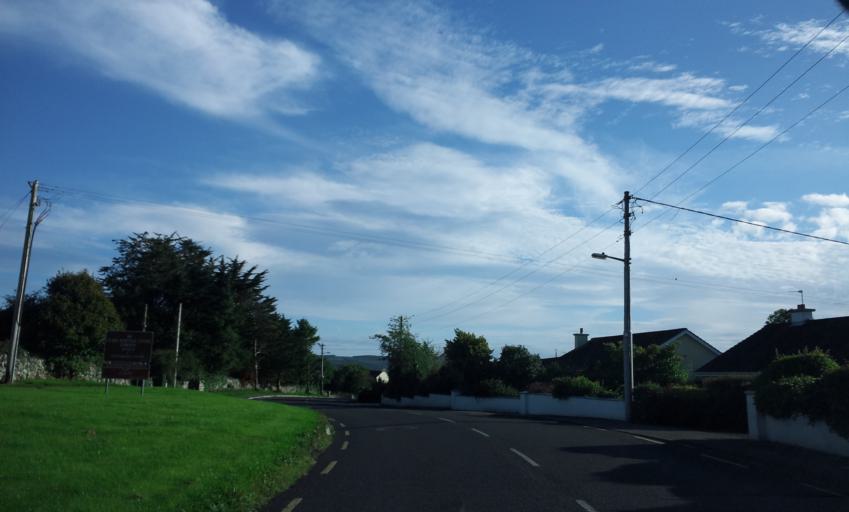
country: IE
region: Munster
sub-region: An Clar
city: Ennis
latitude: 52.9491
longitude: -9.0679
